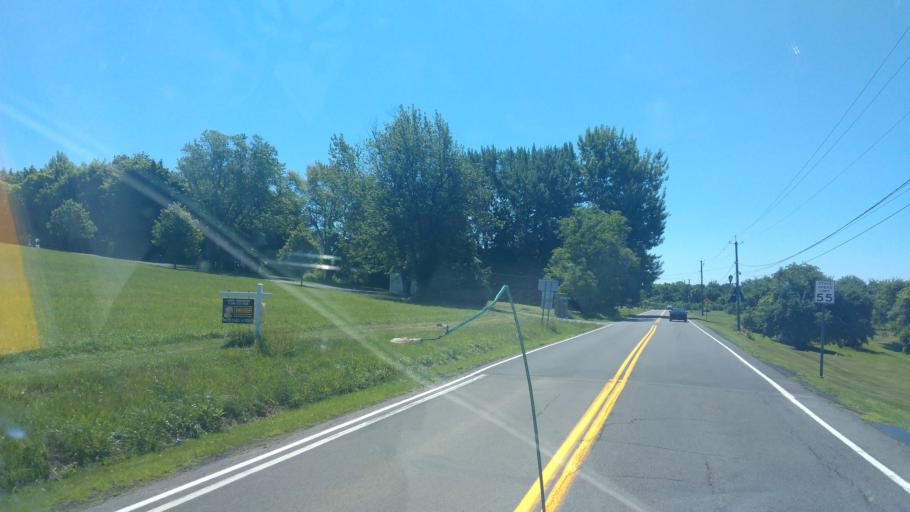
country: US
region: New York
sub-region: Wayne County
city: Sodus
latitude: 43.2541
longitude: -76.9939
